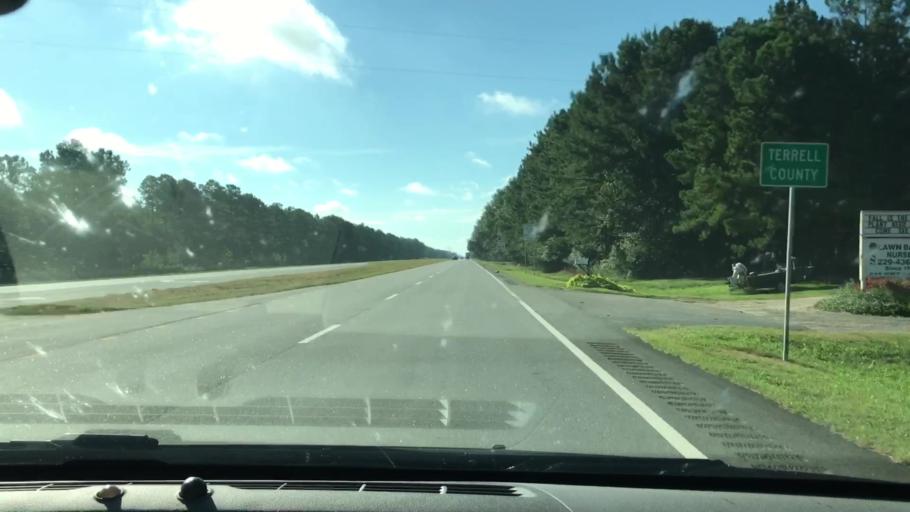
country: US
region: Georgia
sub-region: Lee County
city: Leesburg
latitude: 31.6853
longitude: -84.3058
